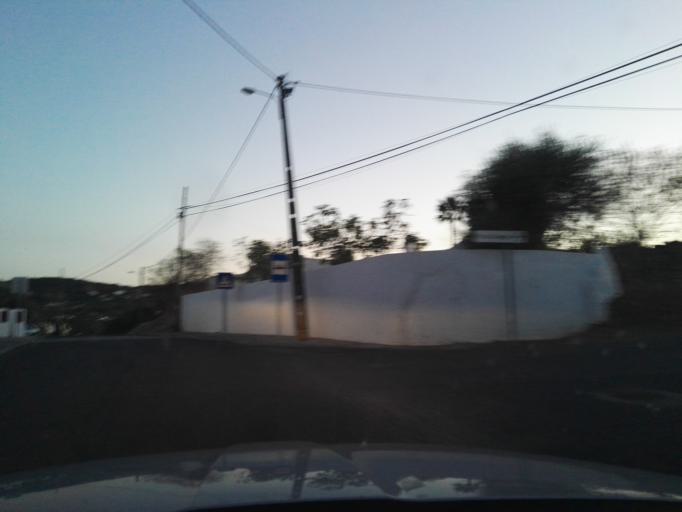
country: PT
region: Faro
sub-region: Sao Bras de Alportel
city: Sao Bras de Alportel
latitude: 37.1536
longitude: -7.9319
